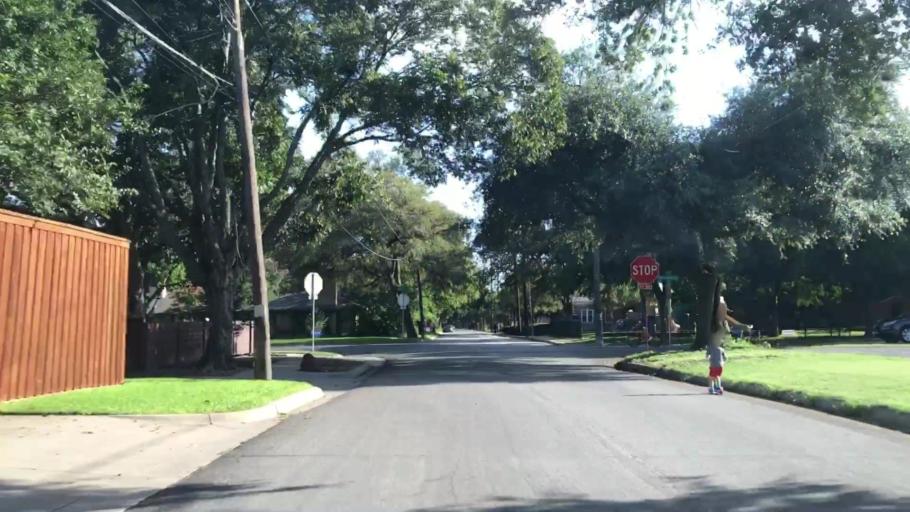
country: US
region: Texas
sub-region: Dallas County
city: Highland Park
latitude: 32.8274
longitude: -96.7602
